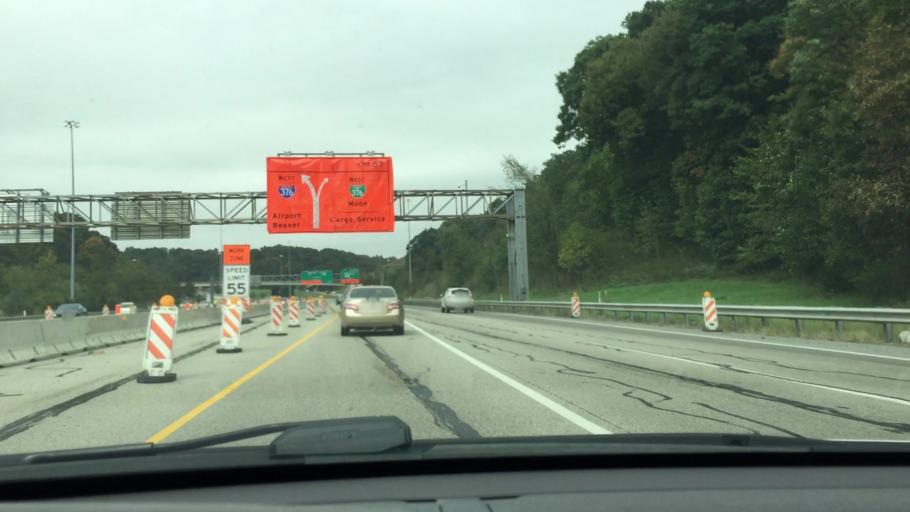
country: US
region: Pennsylvania
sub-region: Allegheny County
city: Enlow
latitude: 40.4628
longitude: -80.1934
